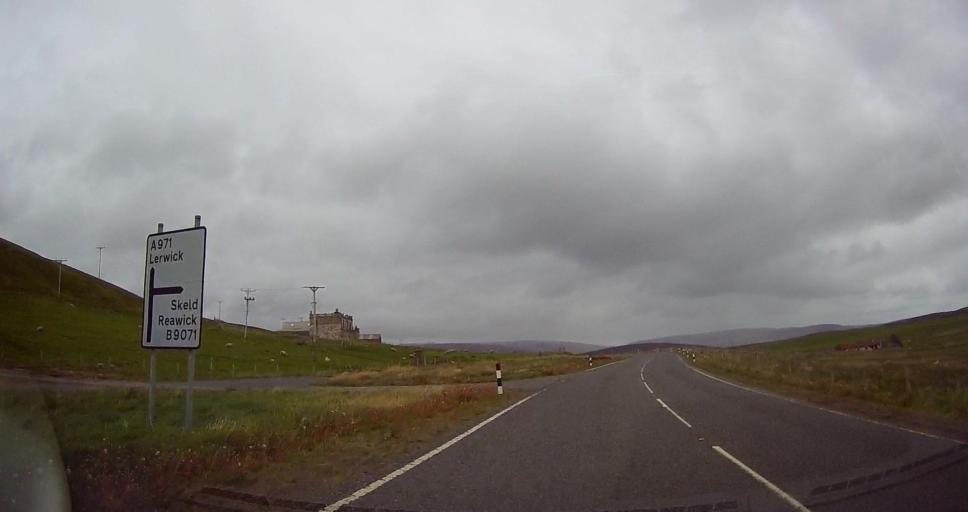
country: GB
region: Scotland
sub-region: Shetland Islands
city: Lerwick
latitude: 60.2573
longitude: -1.4403
